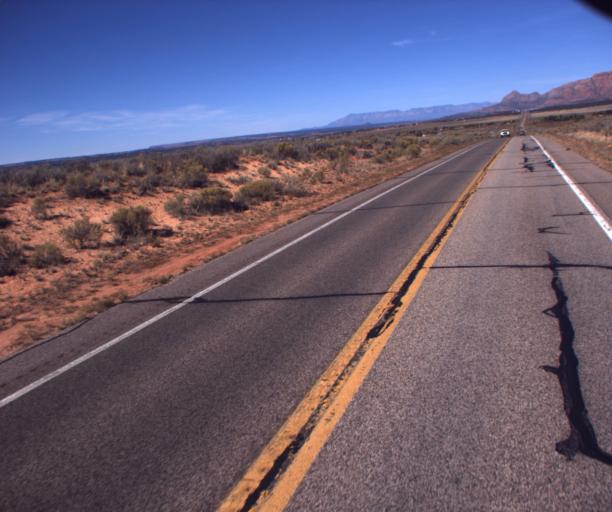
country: US
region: Arizona
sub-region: Mohave County
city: Colorado City
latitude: 36.9148
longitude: -112.9308
